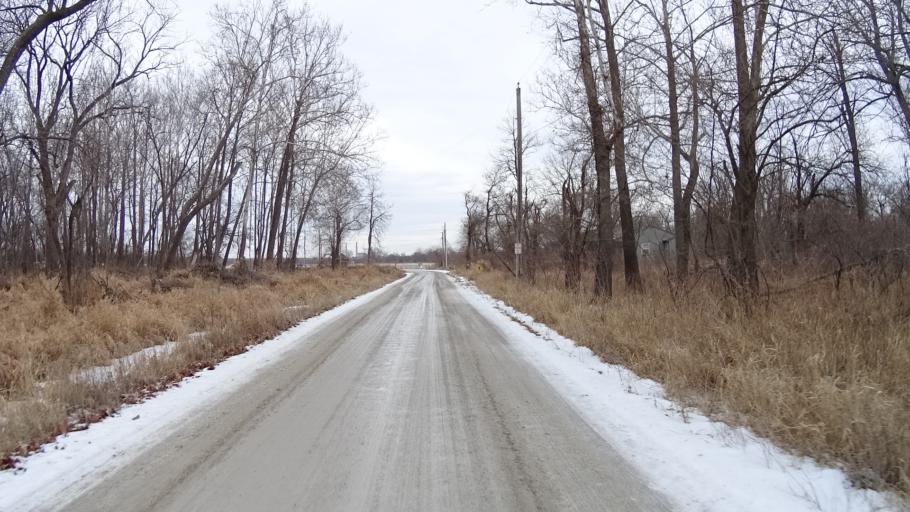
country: US
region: Nebraska
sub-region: Sarpy County
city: Bellevue
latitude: 41.1751
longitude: -95.8917
